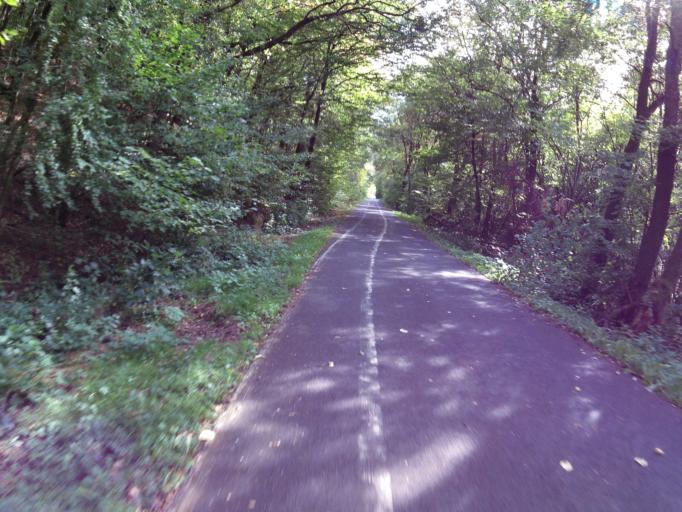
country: DE
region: Rheinland-Pfalz
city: Winterscheid
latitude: 50.2325
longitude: 6.2605
